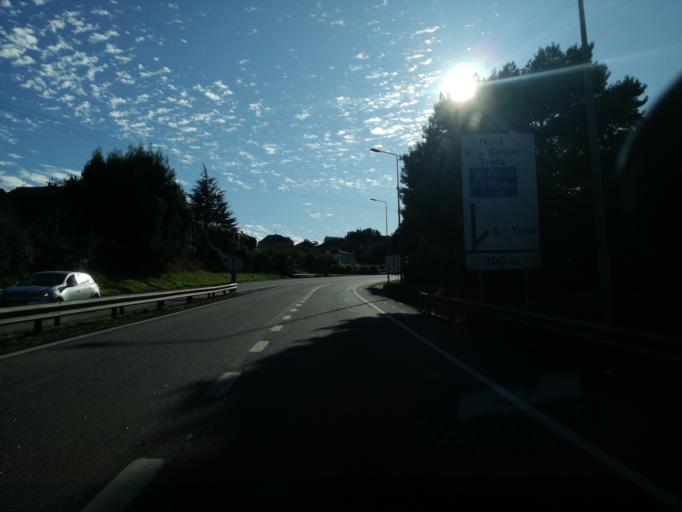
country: PT
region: Porto
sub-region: Santo Tirso
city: Sao Miguel do Couto
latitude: 41.3282
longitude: -8.4733
